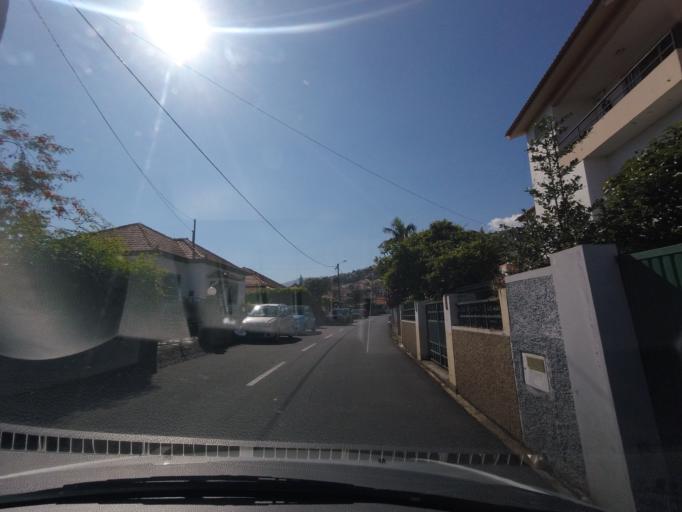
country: PT
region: Madeira
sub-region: Funchal
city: Nossa Senhora do Monte
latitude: 32.6656
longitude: -16.9077
